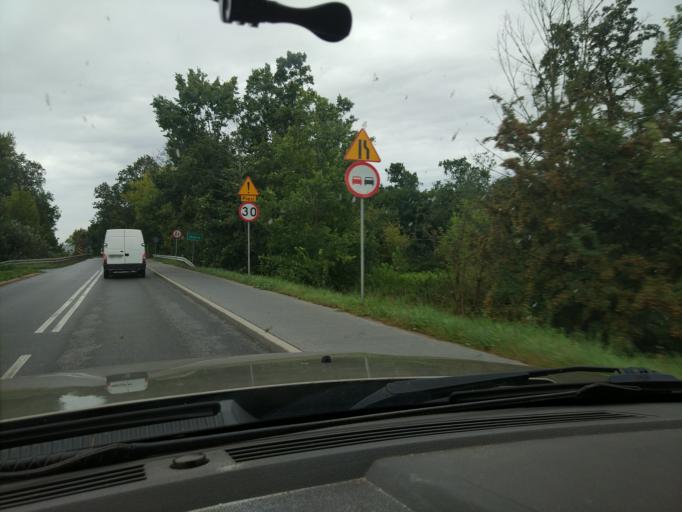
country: PL
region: Masovian Voivodeship
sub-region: Powiat pruszkowski
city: Brwinow
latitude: 52.1843
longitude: 20.7505
